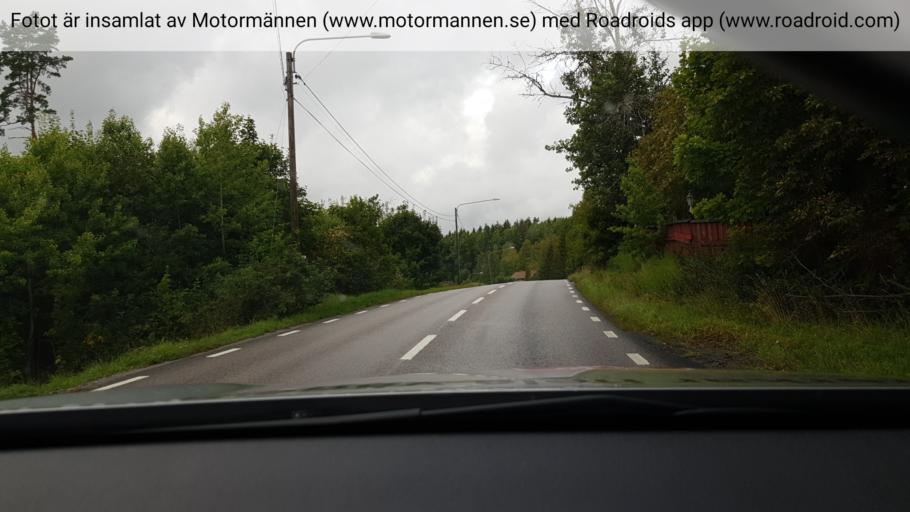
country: SE
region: Stockholm
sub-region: Norrtalje Kommun
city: Rimbo
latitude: 59.7331
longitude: 18.4168
